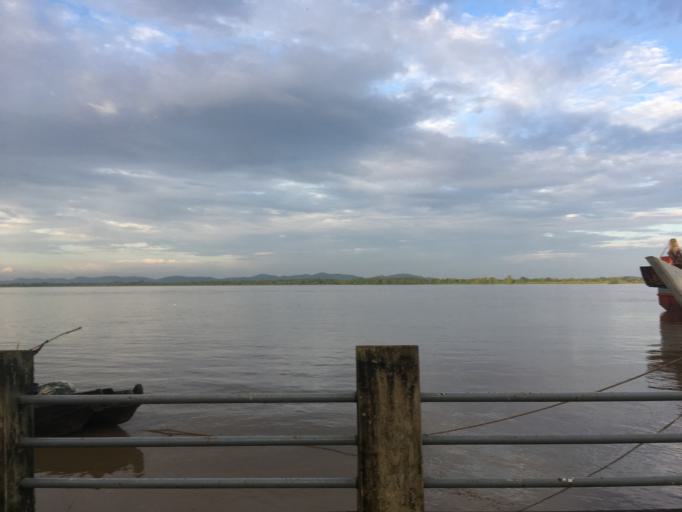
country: MM
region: Mon
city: Mawlamyine
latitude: 16.4649
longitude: 97.6224
